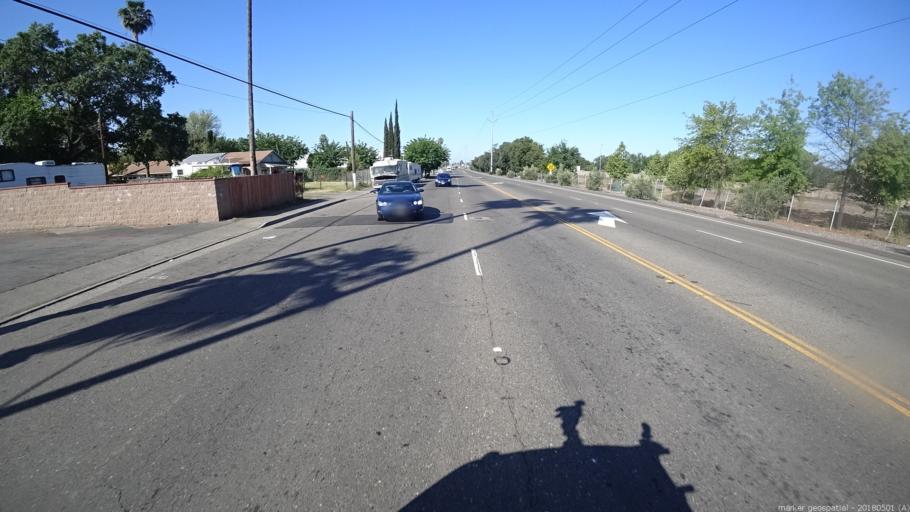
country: US
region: California
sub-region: Sacramento County
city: Arden-Arcade
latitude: 38.6360
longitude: -121.3859
